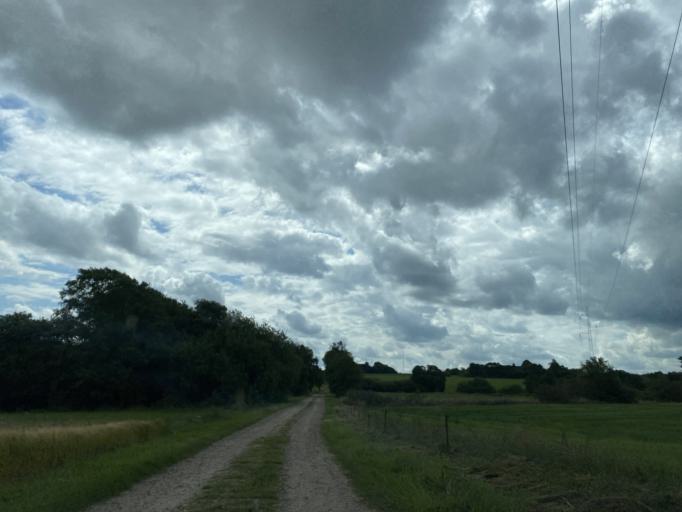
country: DK
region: Central Jutland
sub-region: Silkeborg Kommune
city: Silkeborg
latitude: 56.2176
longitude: 9.5699
